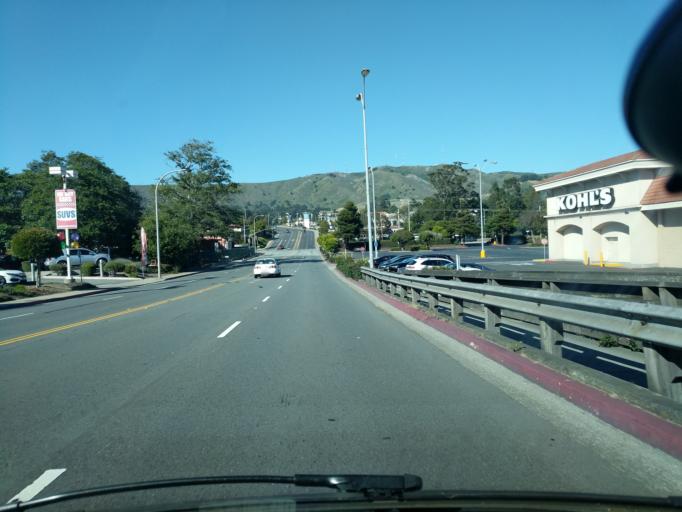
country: US
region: California
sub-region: San Mateo County
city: Colma
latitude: 37.6756
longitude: -122.4597
